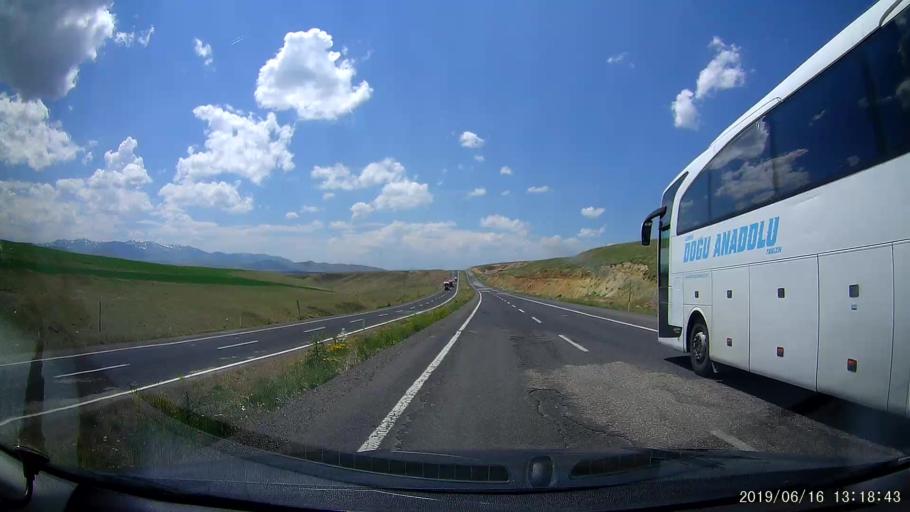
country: TR
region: Agri
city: Taslicay
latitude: 39.6314
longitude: 43.4252
